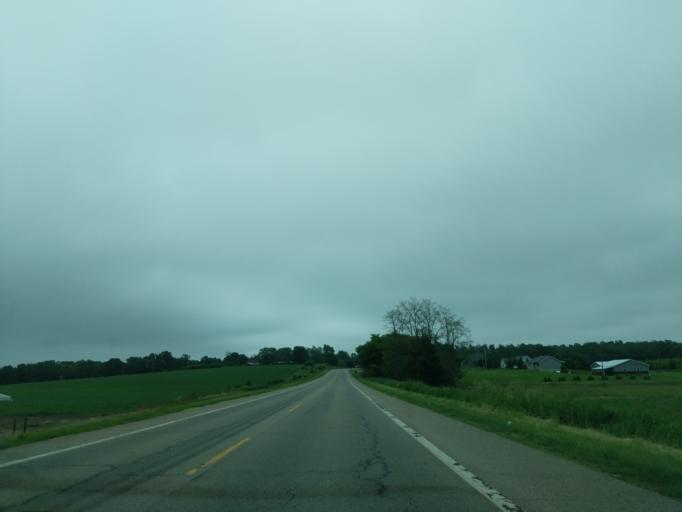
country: US
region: Michigan
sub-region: Hillsdale County
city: Litchfield
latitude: 42.0290
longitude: -84.7168
